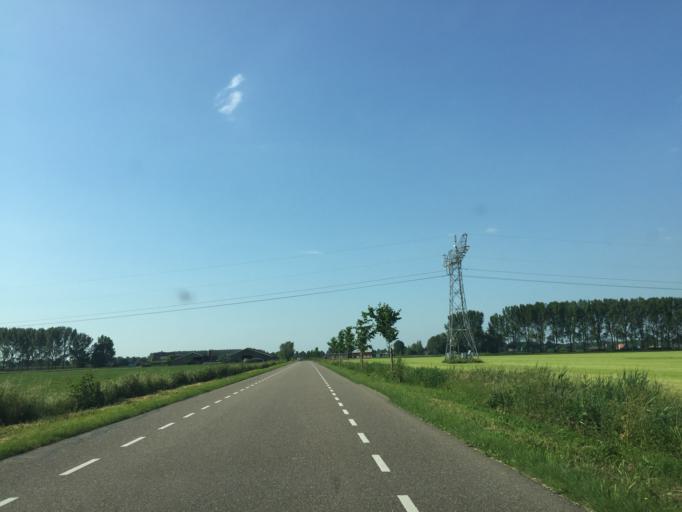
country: NL
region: Gelderland
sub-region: Gemeente Tiel
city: Tiel
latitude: 51.8697
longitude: 5.4857
